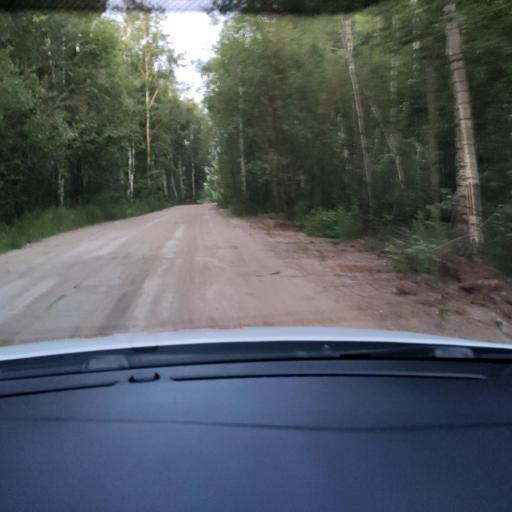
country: RU
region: Tatarstan
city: Stolbishchi
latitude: 55.7085
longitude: 49.1852
